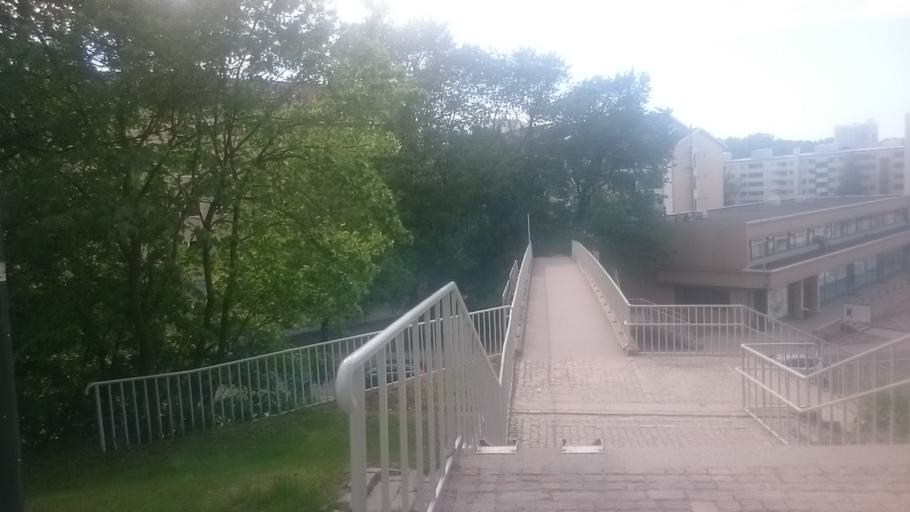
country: FI
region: Varsinais-Suomi
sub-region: Turku
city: Turku
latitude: 60.4423
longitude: 22.2586
